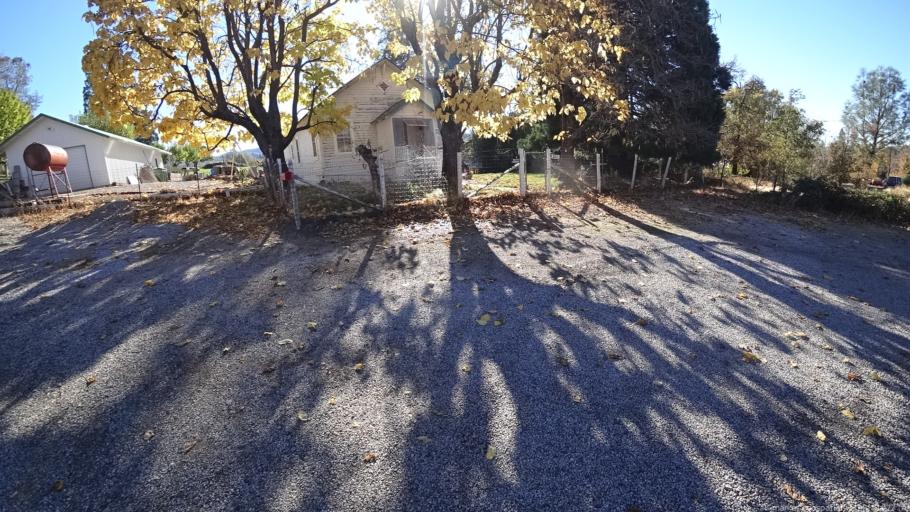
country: US
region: California
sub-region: Shasta County
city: Burney
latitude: 40.8449
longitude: -121.9220
